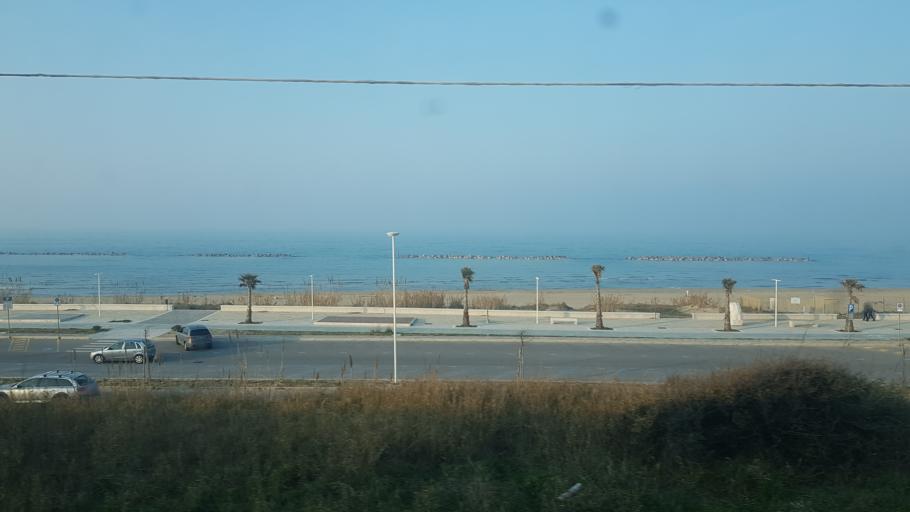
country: IT
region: Molise
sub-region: Provincia di Campobasso
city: Termoli
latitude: 42.0071
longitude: 14.9677
